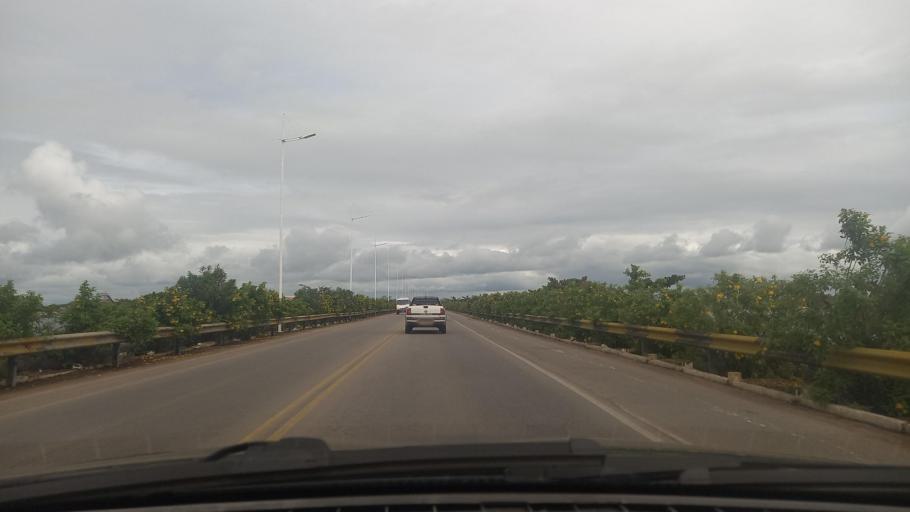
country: BR
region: Bahia
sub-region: Paulo Afonso
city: Paulo Afonso
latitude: -9.4272
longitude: -38.2292
